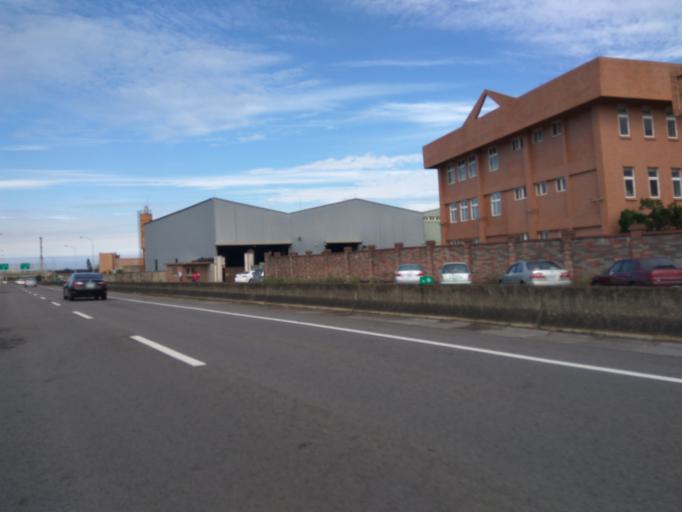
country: TW
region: Taiwan
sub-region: Hsinchu
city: Zhubei
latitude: 25.0270
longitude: 121.0587
